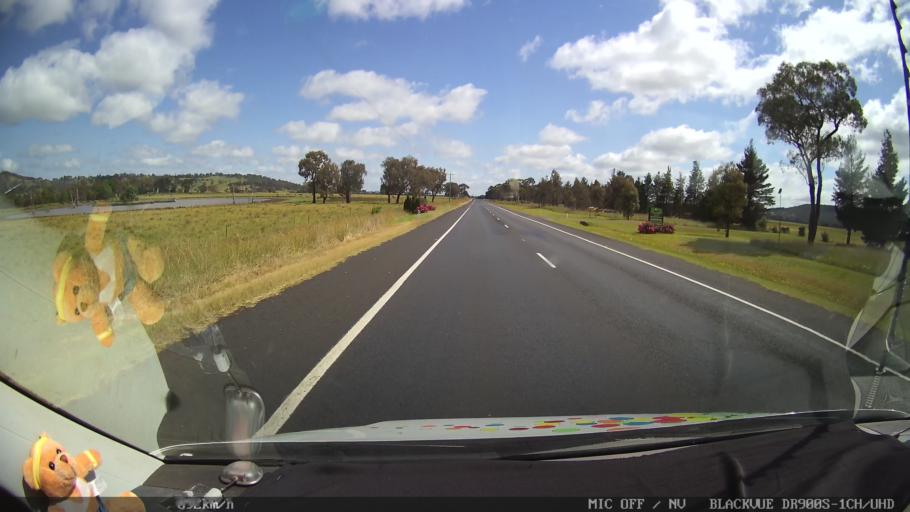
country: AU
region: New South Wales
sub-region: Glen Innes Severn
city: Glen Innes
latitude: -29.8749
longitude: 151.7347
